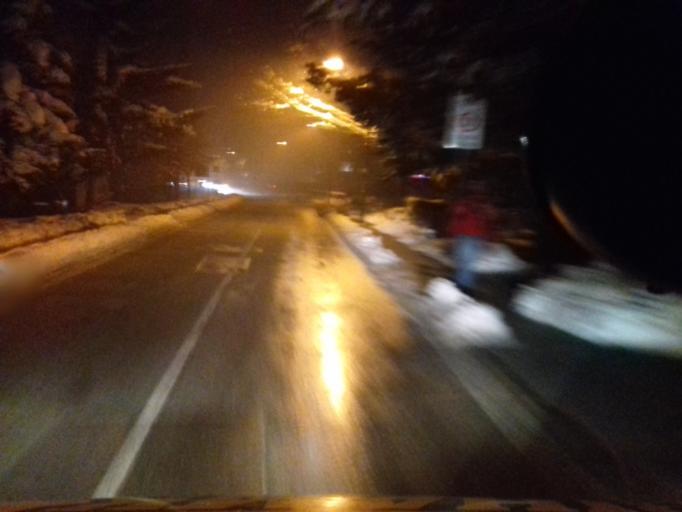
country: BA
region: Federation of Bosnia and Herzegovina
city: Kobilja Glava
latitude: 43.8671
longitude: 18.4203
